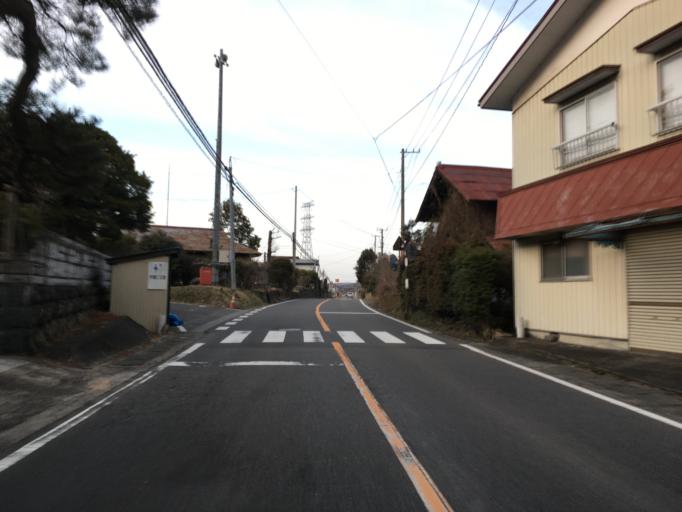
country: JP
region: Ibaraki
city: Daigo
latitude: 36.9221
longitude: 140.4078
